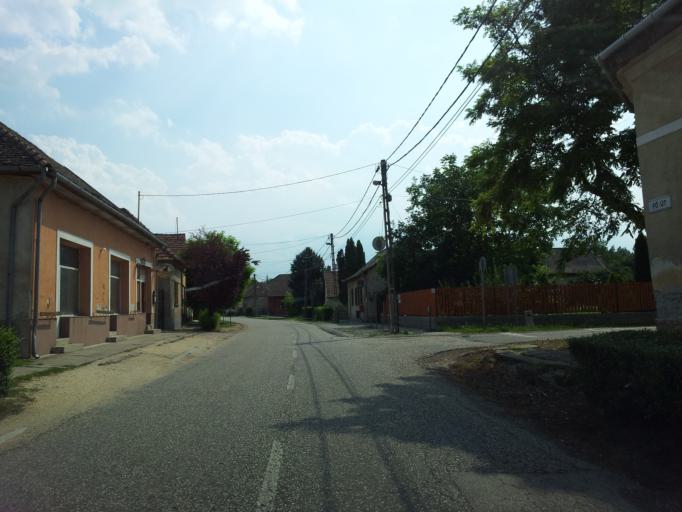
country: HU
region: Pest
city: Szigetujfalu
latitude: 47.2345
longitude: 18.9227
